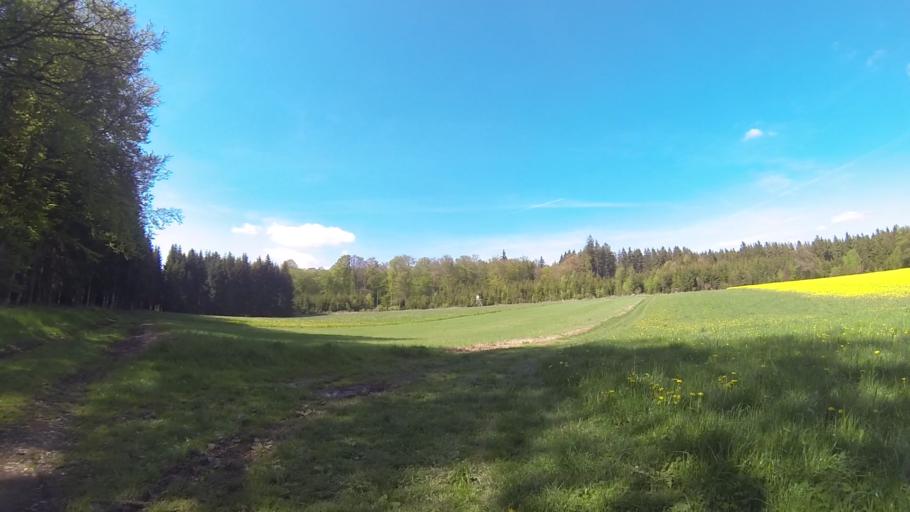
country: DE
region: Baden-Wuerttemberg
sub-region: Regierungsbezirk Stuttgart
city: Bartholoma
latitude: 48.7666
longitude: 10.0193
